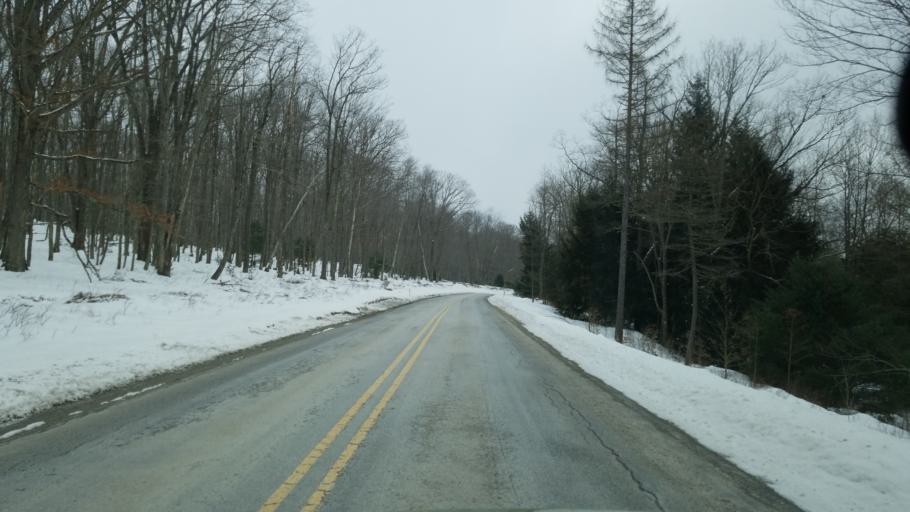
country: US
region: Pennsylvania
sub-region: Clearfield County
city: Shiloh
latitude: 41.2380
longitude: -78.1859
